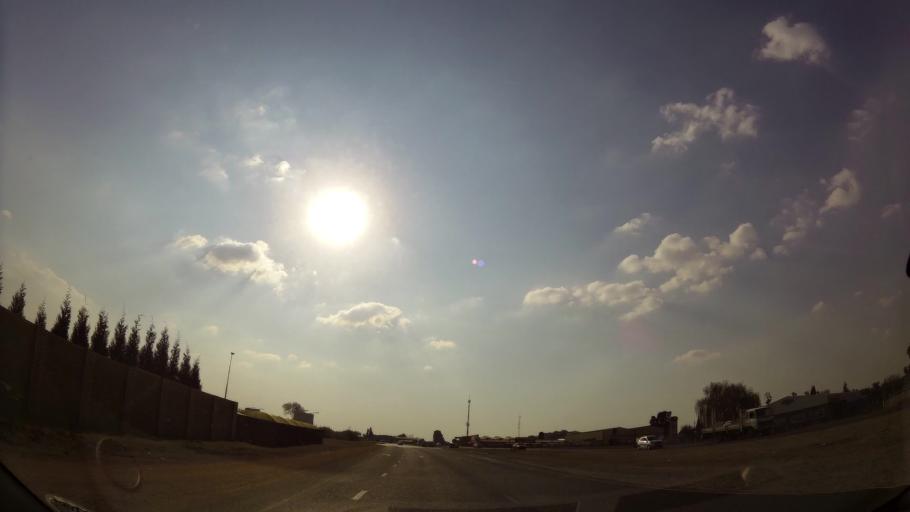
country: ZA
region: Gauteng
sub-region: Ekurhuleni Metropolitan Municipality
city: Benoni
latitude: -26.1256
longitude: 28.2868
